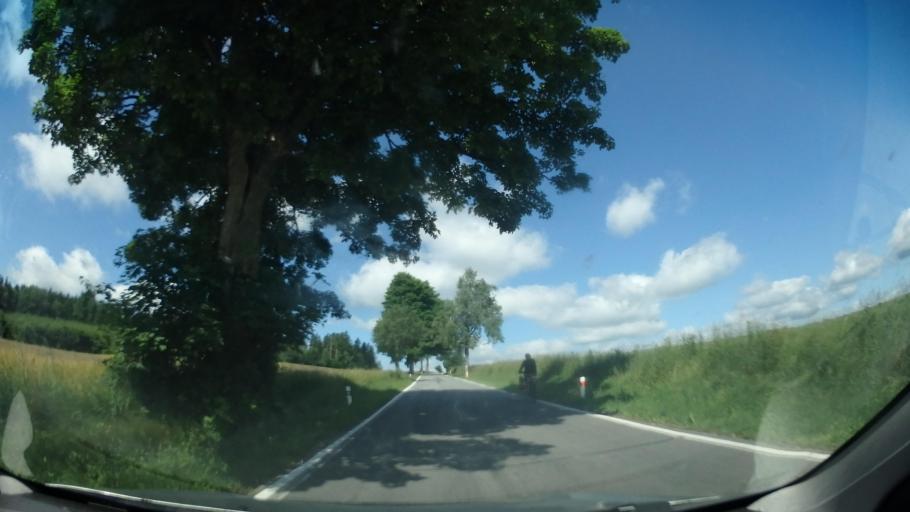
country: CZ
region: Vysocina
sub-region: Okres Zd'ar nad Sazavou
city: Nove Mesto na Morave
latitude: 49.6434
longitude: 16.1150
